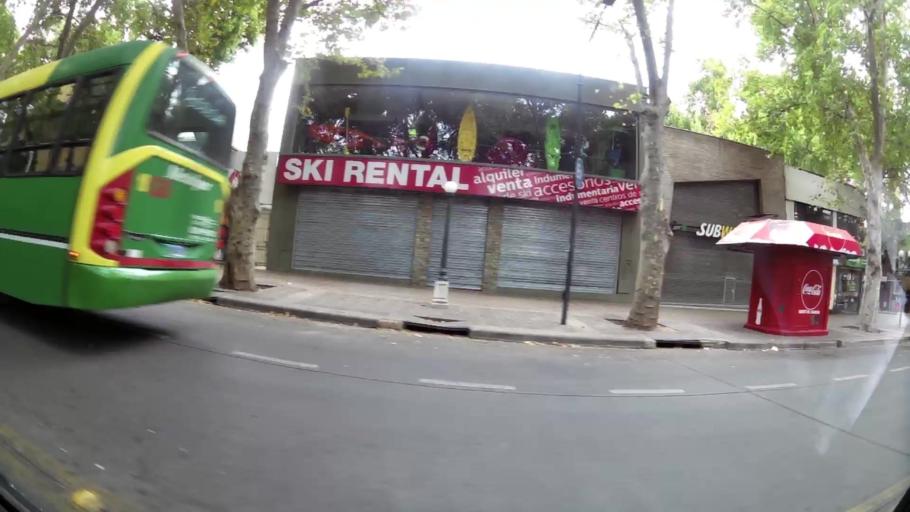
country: AR
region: Mendoza
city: Mendoza
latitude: -32.8851
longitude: -68.8449
